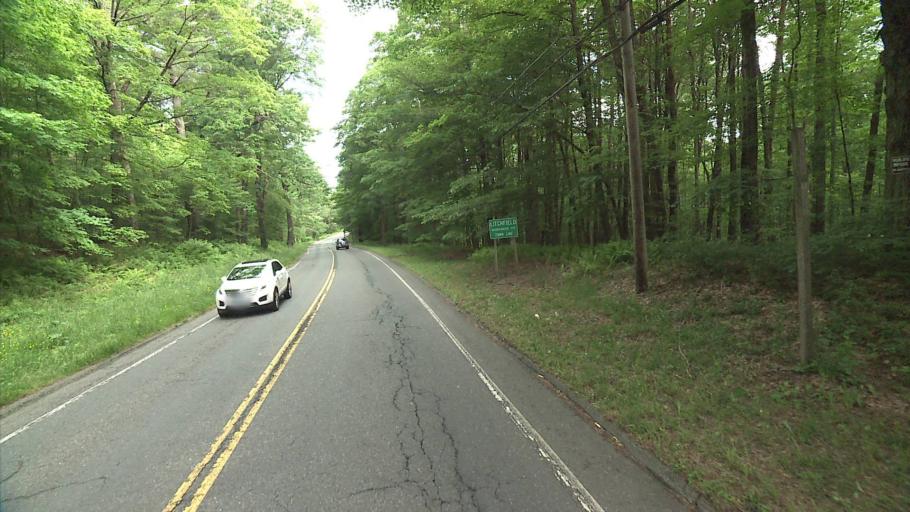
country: US
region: Connecticut
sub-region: Litchfield County
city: Litchfield
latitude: 41.7124
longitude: -73.1852
